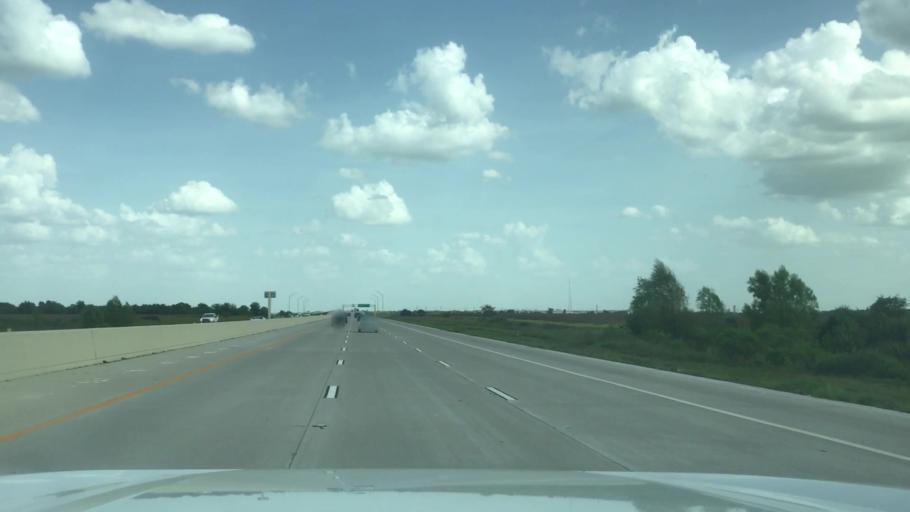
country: US
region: Texas
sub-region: Waller County
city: Waller
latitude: 30.0540
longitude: -95.8837
